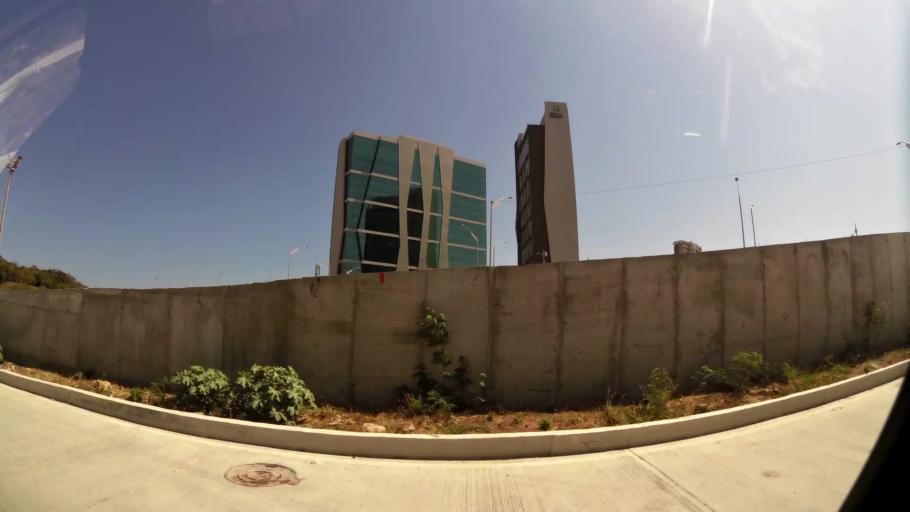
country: CO
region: Atlantico
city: Barranquilla
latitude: 11.0187
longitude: -74.8377
